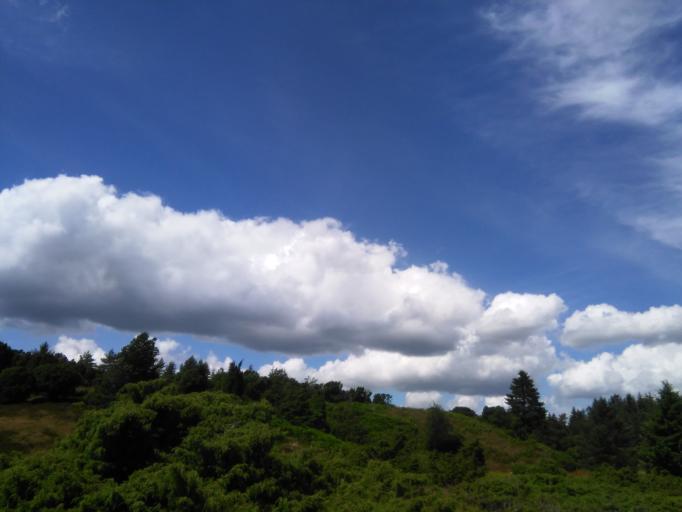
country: DK
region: Central Jutland
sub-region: Silkeborg Kommune
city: Virklund
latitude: 56.0760
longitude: 9.4520
